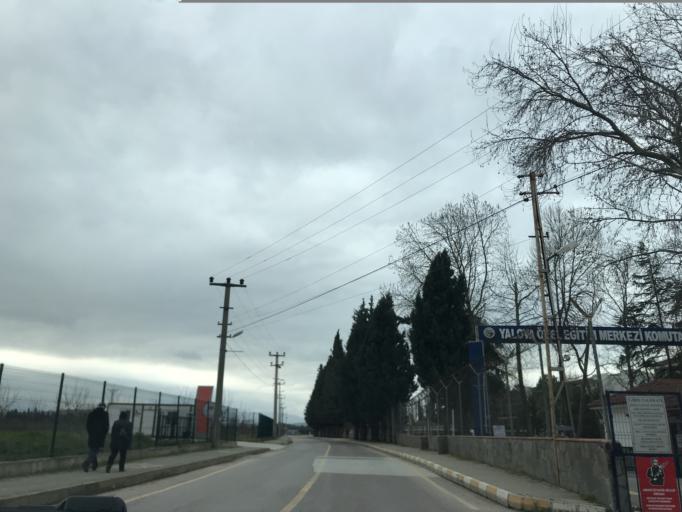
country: TR
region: Yalova
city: Ciftlikkoy
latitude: 40.6637
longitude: 29.3047
